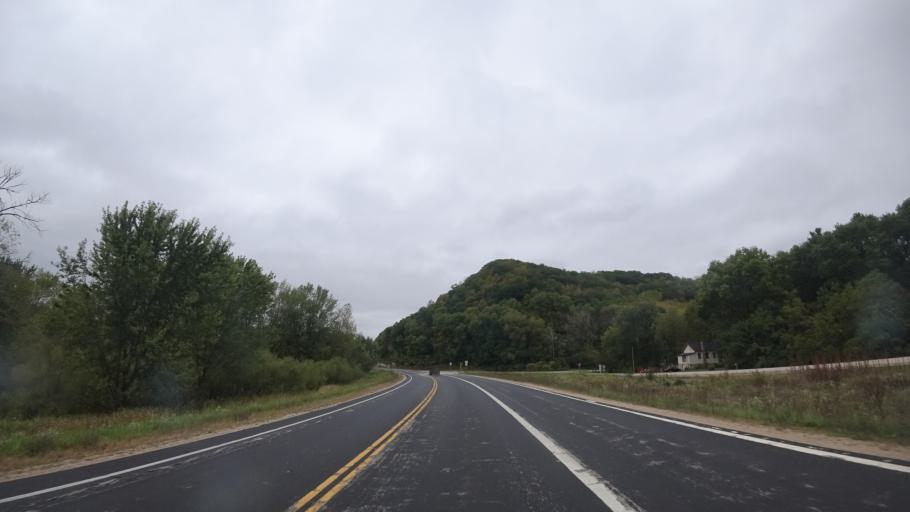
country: US
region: Wisconsin
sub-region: Grant County
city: Boscobel
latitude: 43.1519
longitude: -90.7199
